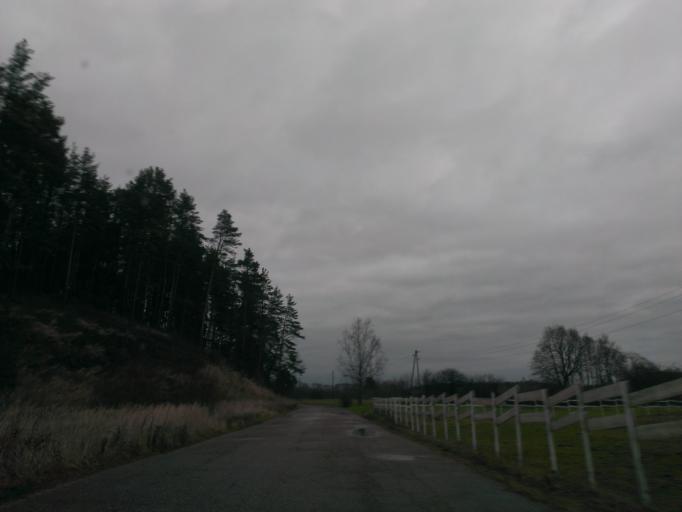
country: LV
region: Adazi
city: Adazi
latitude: 57.0619
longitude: 24.3564
